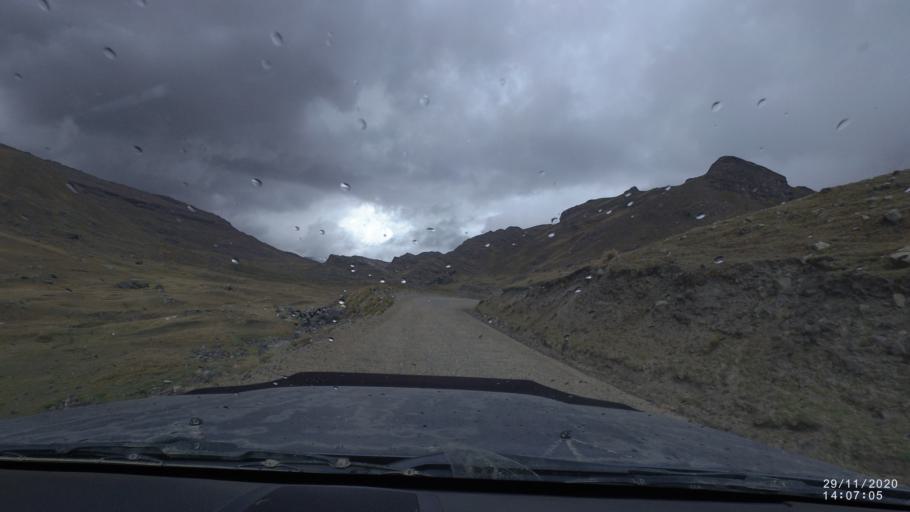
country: BO
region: Cochabamba
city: Sipe Sipe
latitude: -17.2178
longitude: -66.3815
